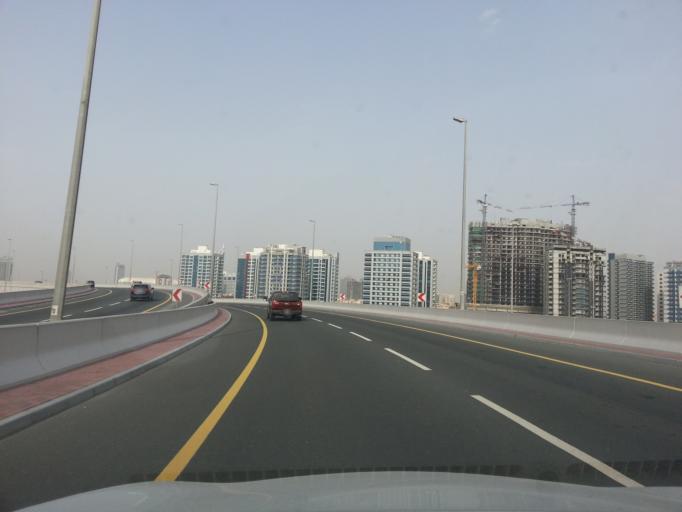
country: AE
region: Dubai
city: Dubai
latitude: 25.0412
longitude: 55.1998
